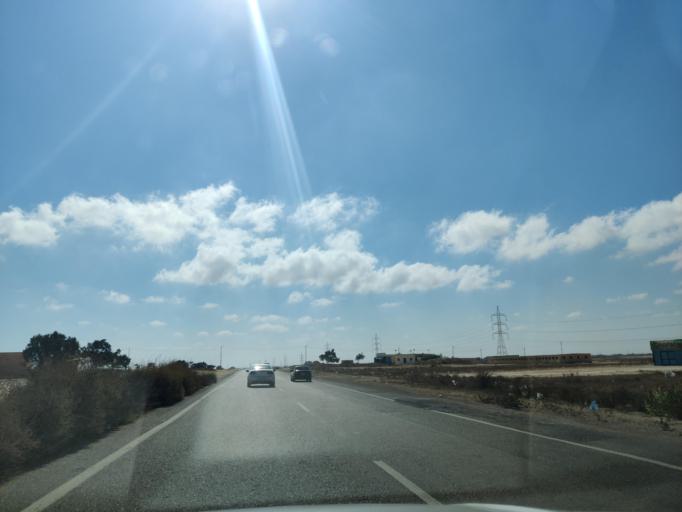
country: EG
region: Muhafazat Matruh
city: Al `Alamayn
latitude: 31.0541
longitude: 28.2797
